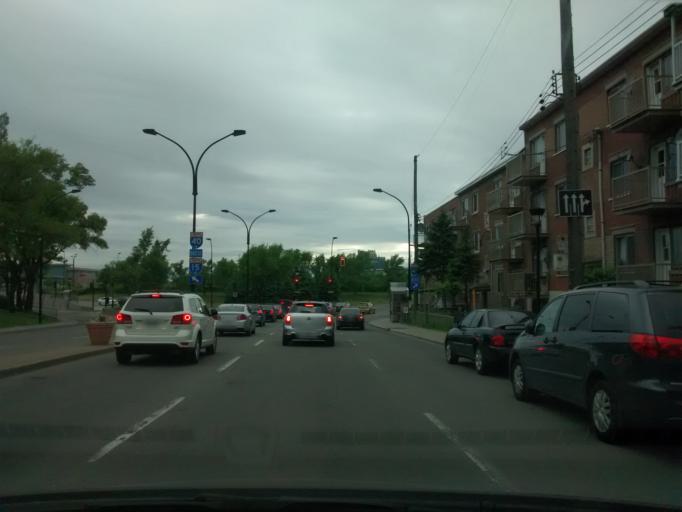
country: CA
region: Quebec
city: Mont-Royal
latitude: 45.5302
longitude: -73.6462
